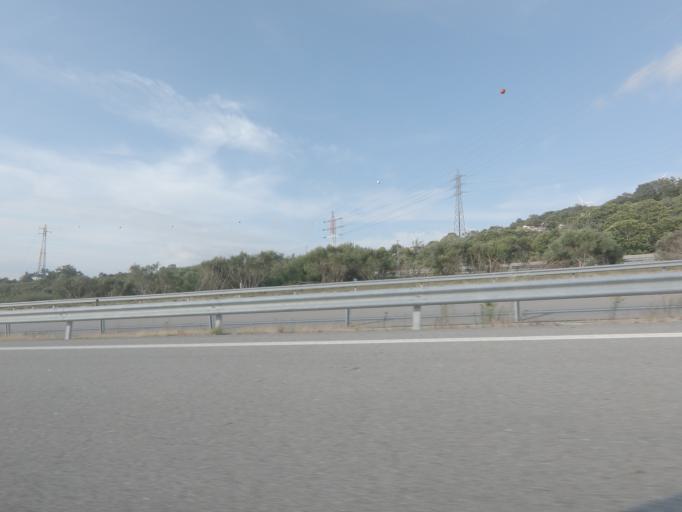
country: PT
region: Vila Real
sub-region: Vila Pouca de Aguiar
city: Vila Pouca de Aguiar
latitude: 41.4762
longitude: -7.6450
